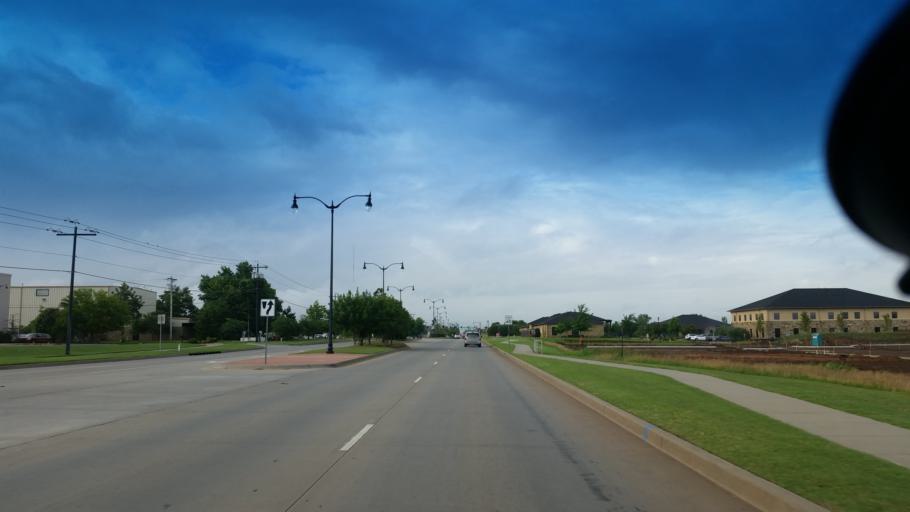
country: US
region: Oklahoma
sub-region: Oklahoma County
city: Edmond
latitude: 35.6320
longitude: -97.4962
